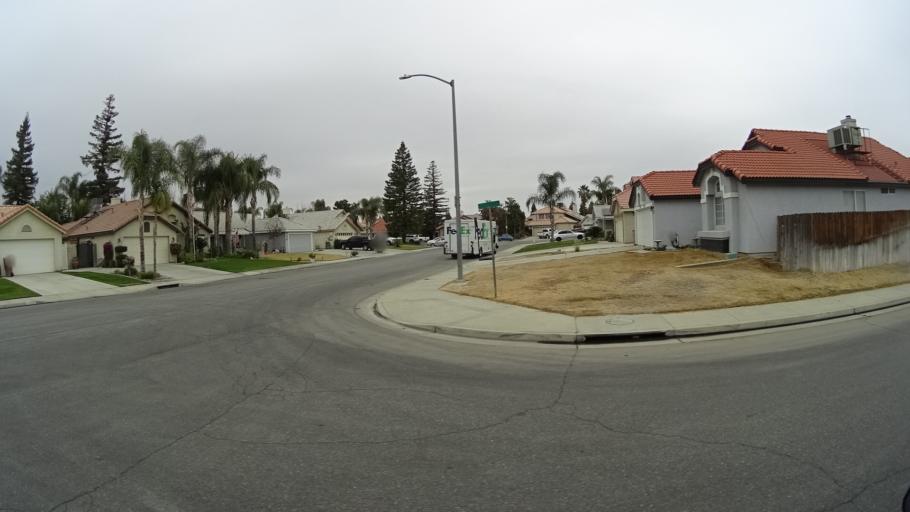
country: US
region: California
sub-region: Kern County
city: Greenfield
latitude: 35.2861
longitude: -119.0447
